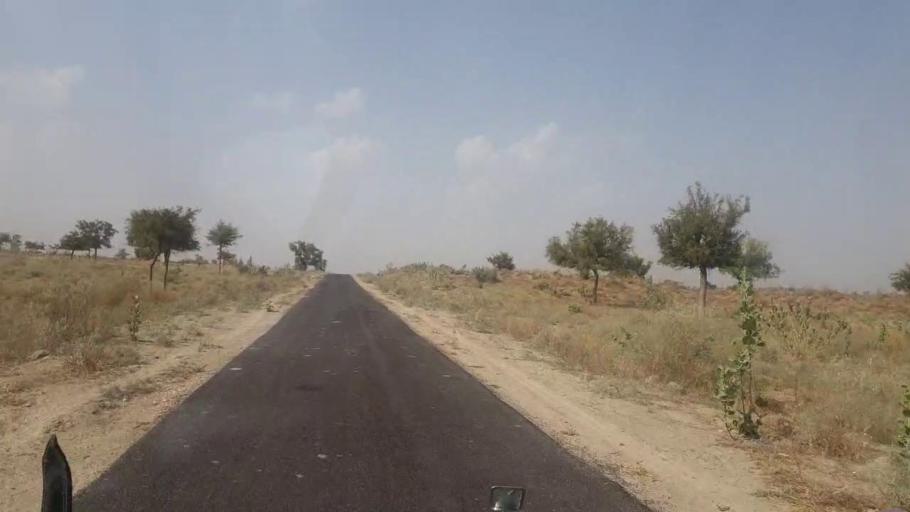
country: PK
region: Sindh
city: Islamkot
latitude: 25.1782
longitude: 70.2876
